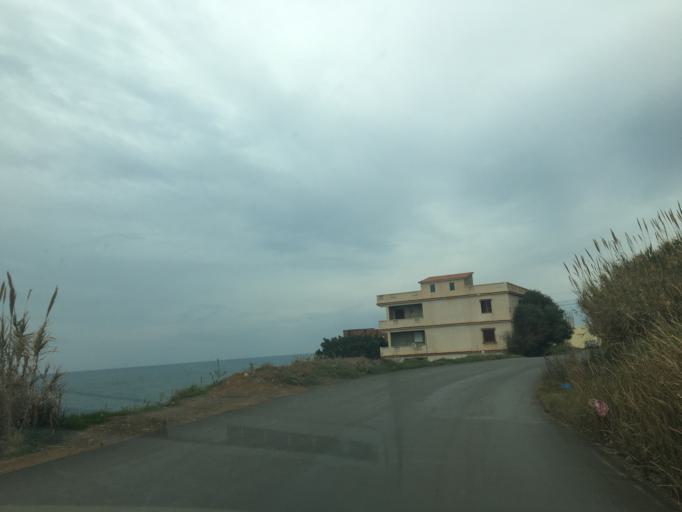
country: DZ
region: Tipaza
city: Tipasa
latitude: 36.6315
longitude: 2.2846
